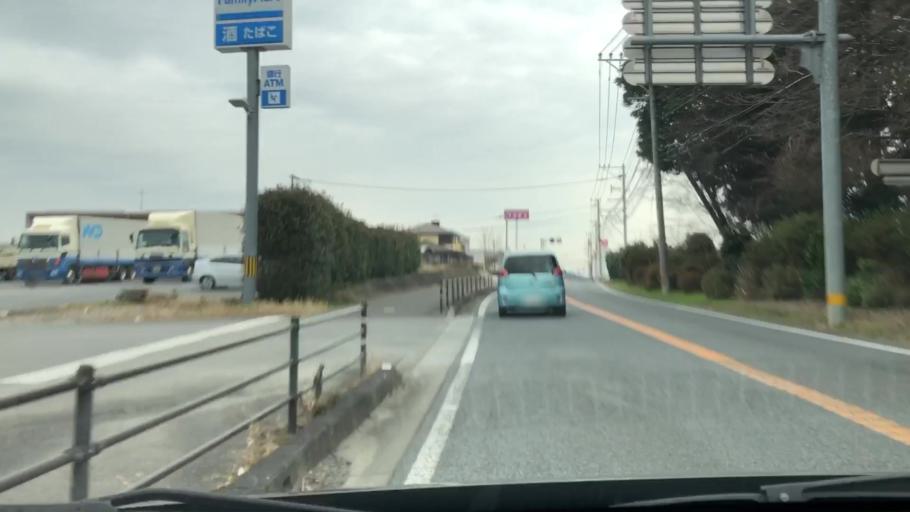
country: JP
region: Oita
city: Takedamachi
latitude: 32.9927
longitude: 131.6129
